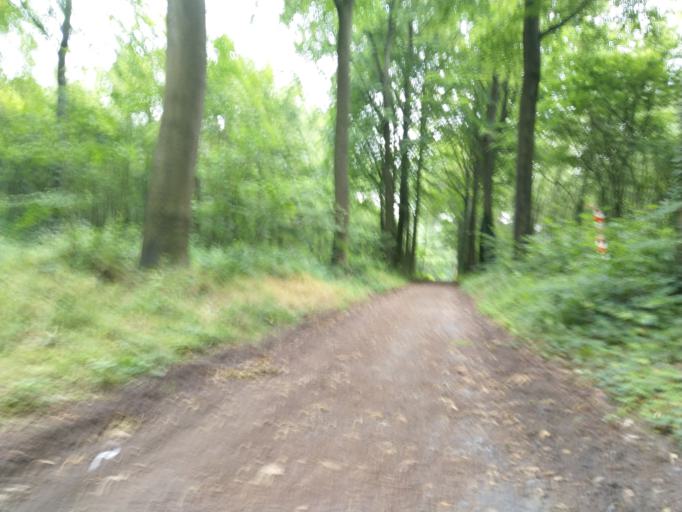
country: BE
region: Wallonia
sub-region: Province du Hainaut
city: Saint-Ghislain
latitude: 50.4877
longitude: 3.8438
